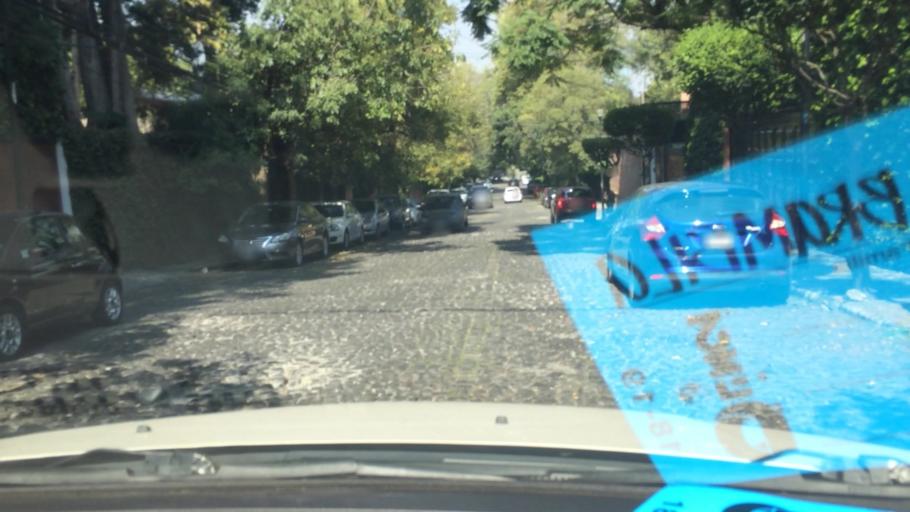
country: MX
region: Mexico City
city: Alvaro Obregon
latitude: 19.3491
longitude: -99.1943
